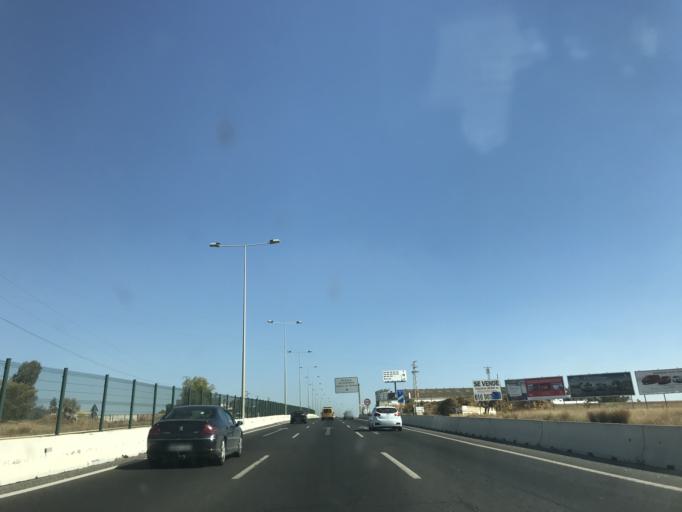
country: ES
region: Andalusia
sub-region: Provincia de Sevilla
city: Alcala de Guadaira
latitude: 37.3543
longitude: -5.8552
